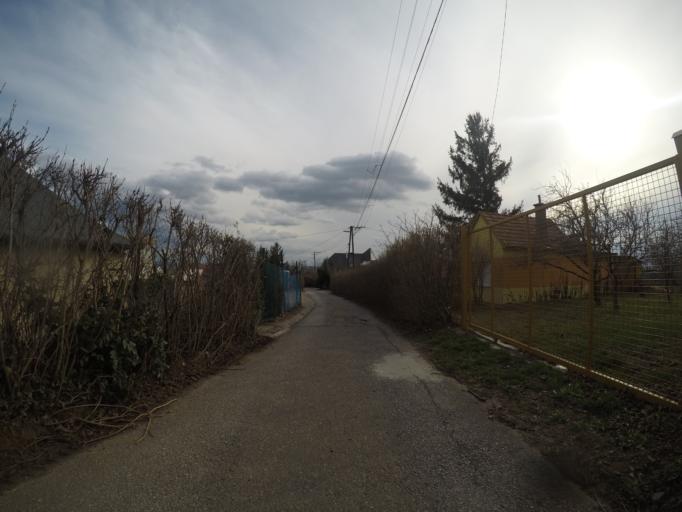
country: HU
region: Baranya
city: Pecs
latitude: 46.0916
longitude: 18.2007
